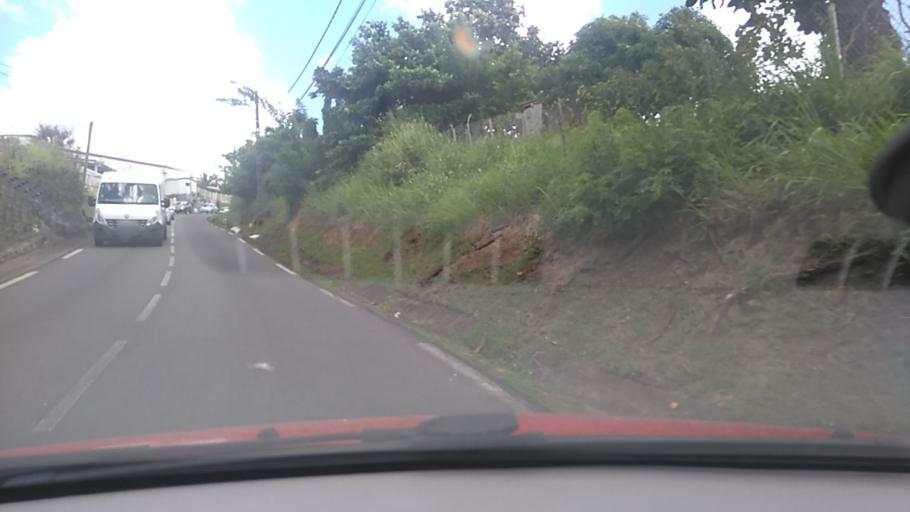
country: MQ
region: Martinique
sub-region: Martinique
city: Saint-Esprit
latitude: 14.5649
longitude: -60.9388
